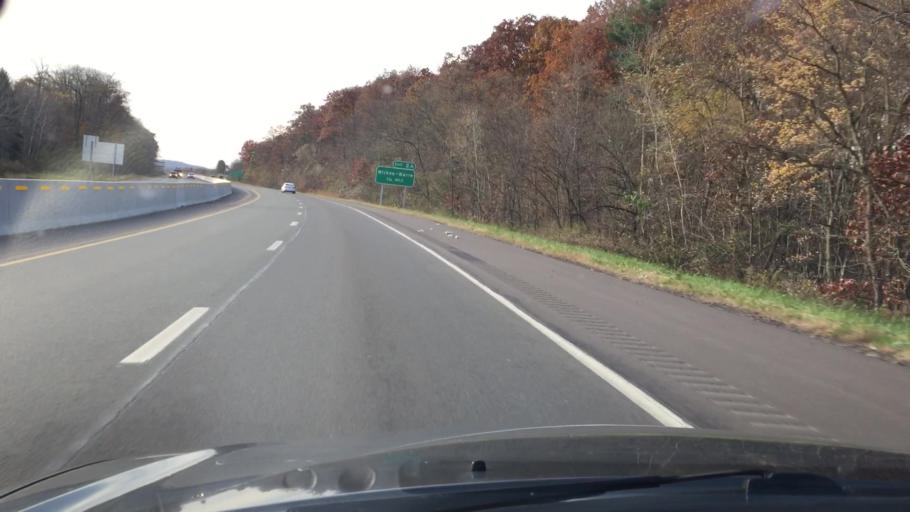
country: US
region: Pennsylvania
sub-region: Luzerne County
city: Ashley
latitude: 41.2032
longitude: -75.9336
